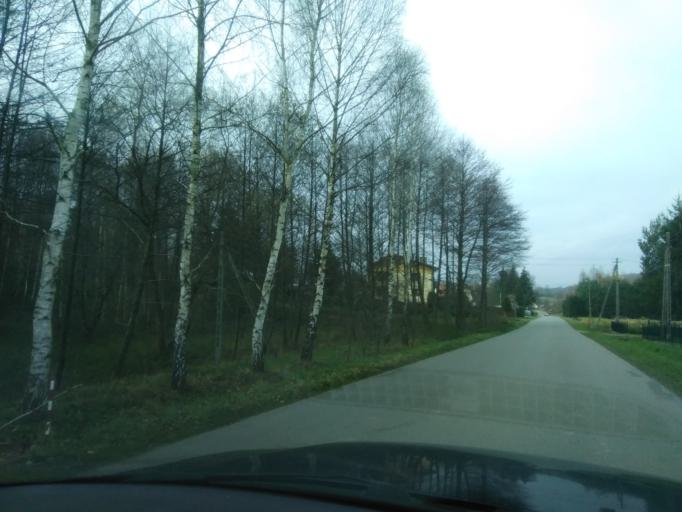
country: PL
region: Subcarpathian Voivodeship
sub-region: Powiat krosnienski
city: Odrzykon
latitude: 49.7727
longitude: 21.7823
